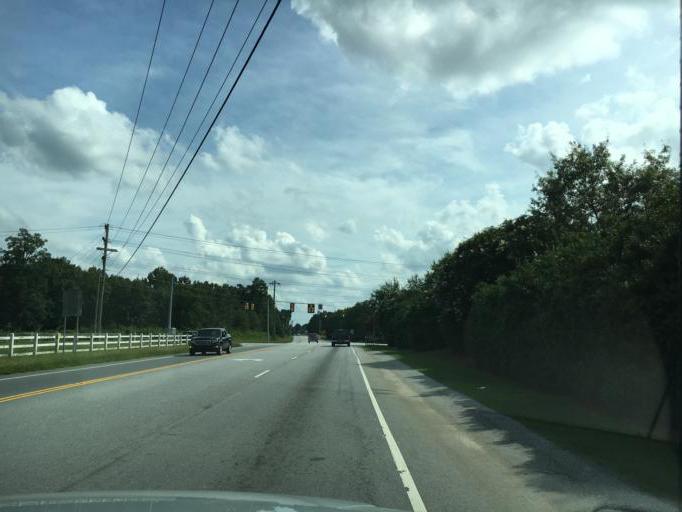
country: US
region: South Carolina
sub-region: Greenville County
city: Five Forks
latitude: 34.8308
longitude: -82.2544
